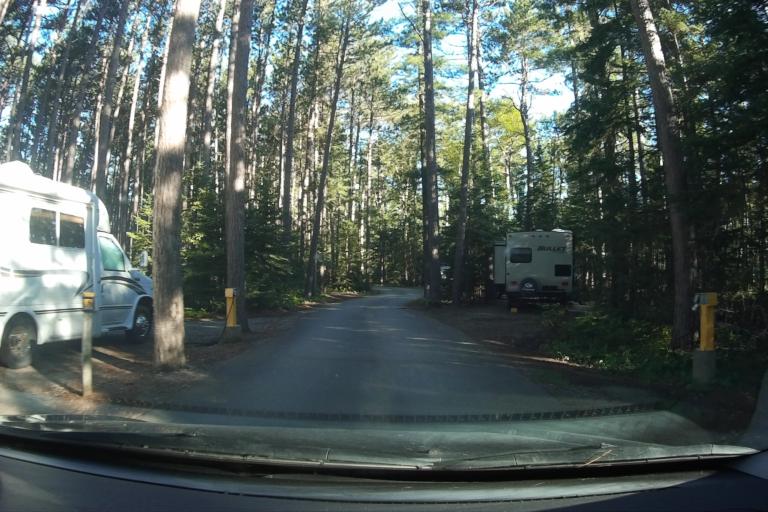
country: CA
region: Ontario
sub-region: Algoma
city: Sault Ste. Marie
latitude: 47.3299
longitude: -84.6128
